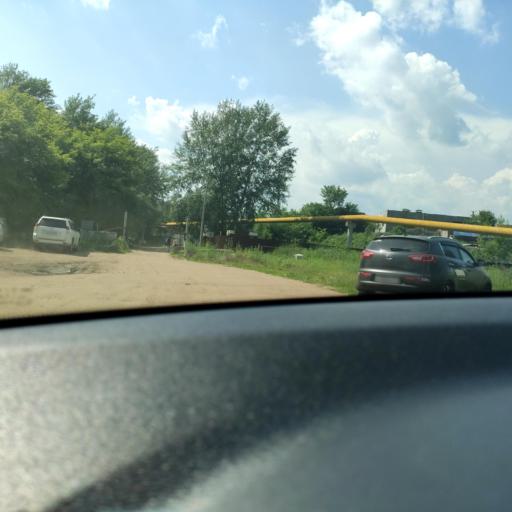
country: RU
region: Samara
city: Smyshlyayevka
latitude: 53.2152
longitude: 50.3350
